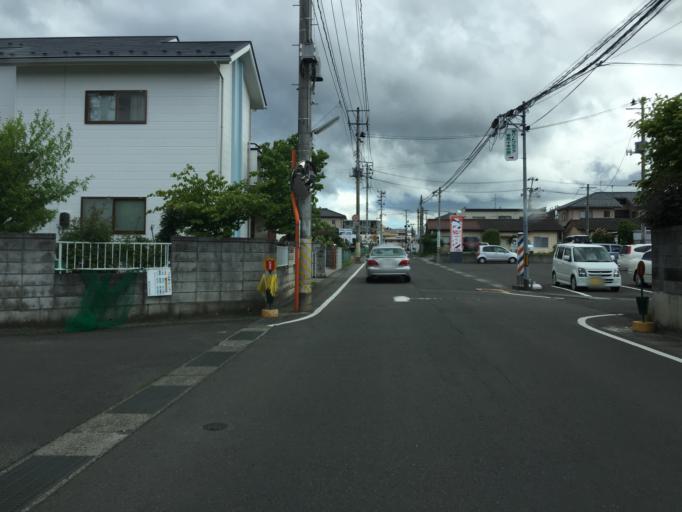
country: JP
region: Fukushima
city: Fukushima-shi
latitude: 37.7647
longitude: 140.4434
